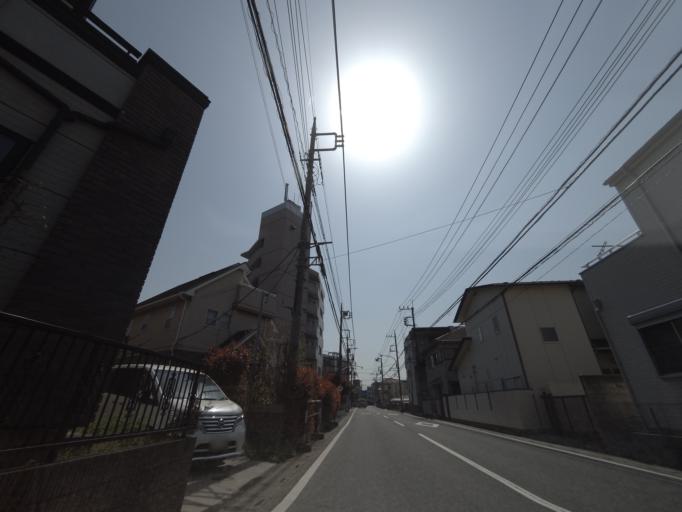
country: JP
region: Saitama
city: Yono
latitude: 35.8502
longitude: 139.6296
